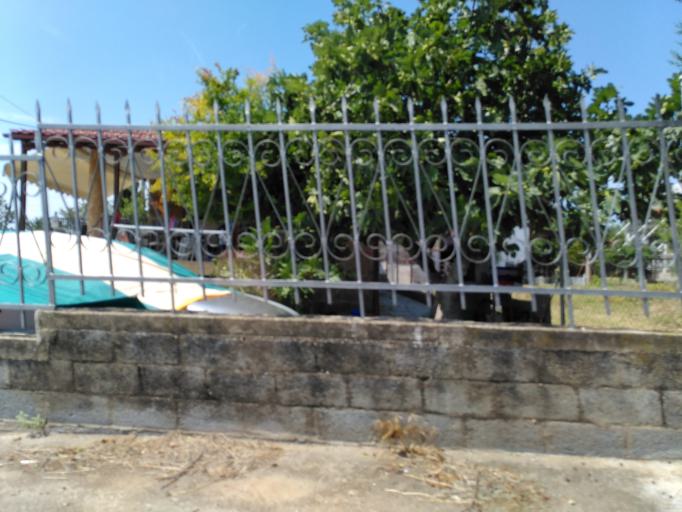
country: GR
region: Central Macedonia
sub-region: Nomos Thessalonikis
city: Nea Michaniona
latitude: 40.4430
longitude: 22.8689
